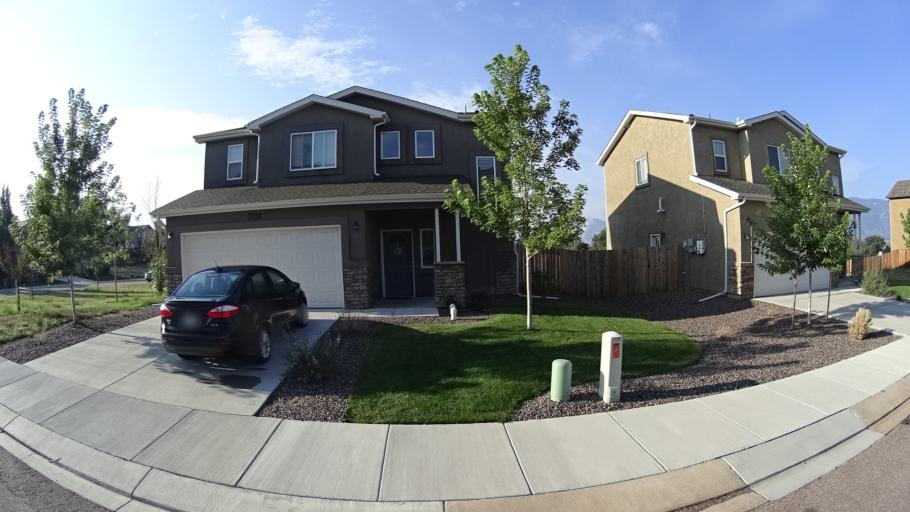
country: US
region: Colorado
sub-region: El Paso County
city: Colorado Springs
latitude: 38.8852
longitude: -104.8047
